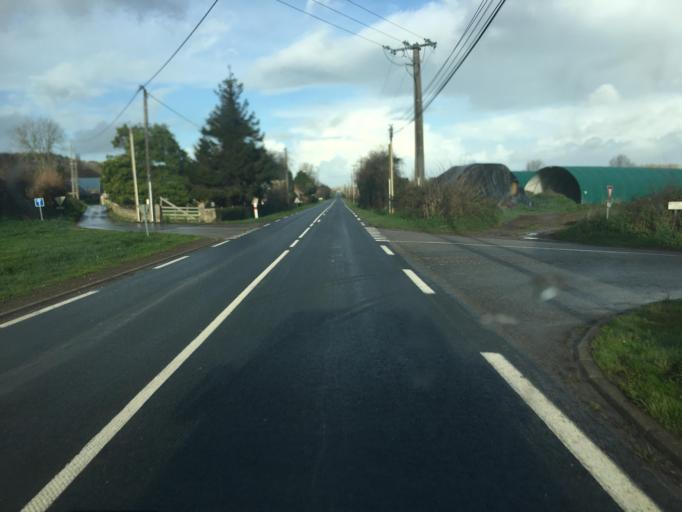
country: FR
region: Lower Normandy
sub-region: Departement de la Manche
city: Quettehou
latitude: 49.6048
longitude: -1.2933
